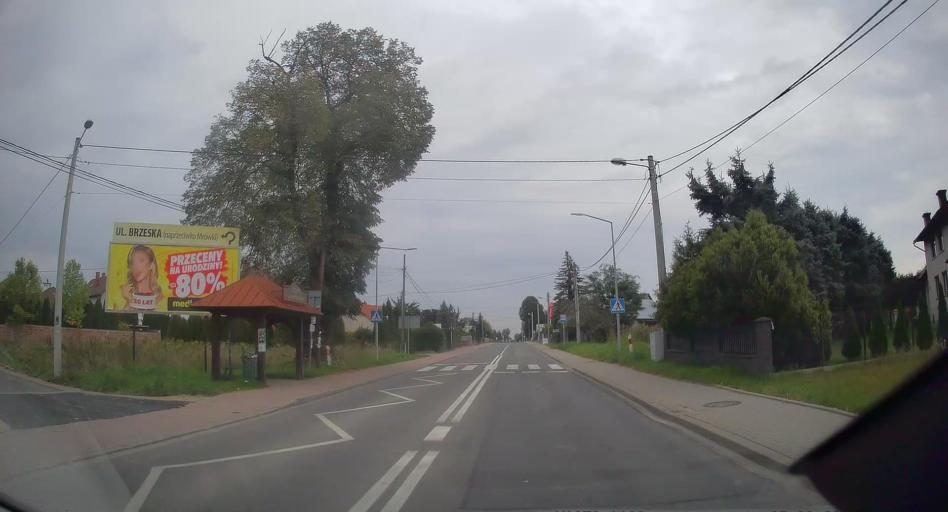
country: PL
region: Lesser Poland Voivodeship
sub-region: Powiat wielicki
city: Niepolomice
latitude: 50.0287
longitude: 20.2057
